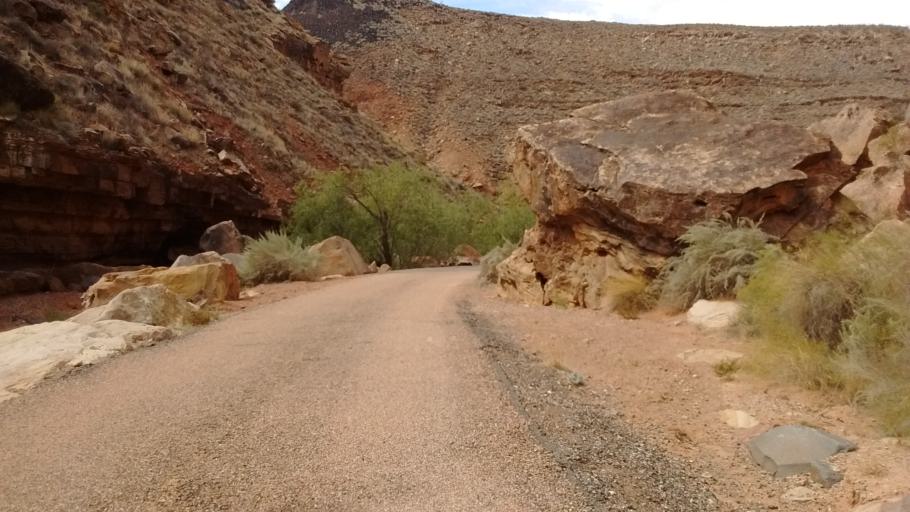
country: US
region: Utah
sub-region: Washington County
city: Washington
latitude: 37.1271
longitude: -113.4815
